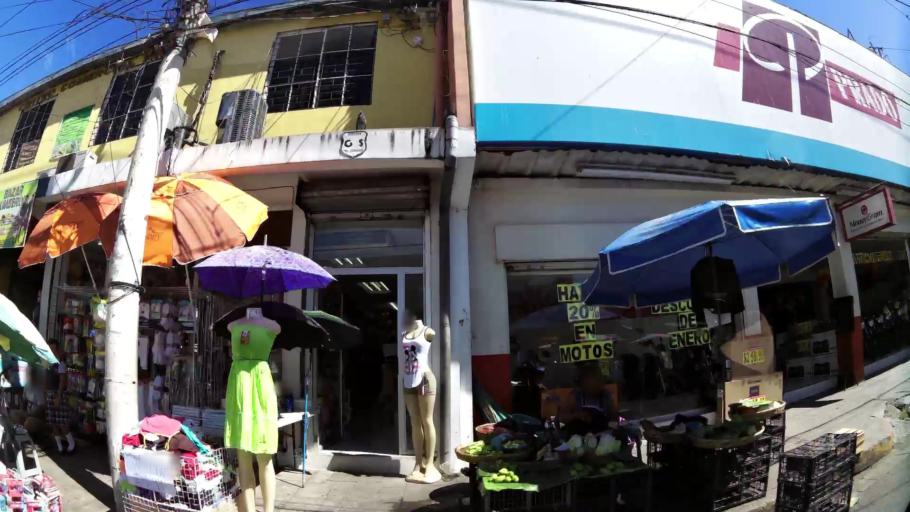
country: SV
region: San Salvador
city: Apopa
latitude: 13.7995
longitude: -89.1786
